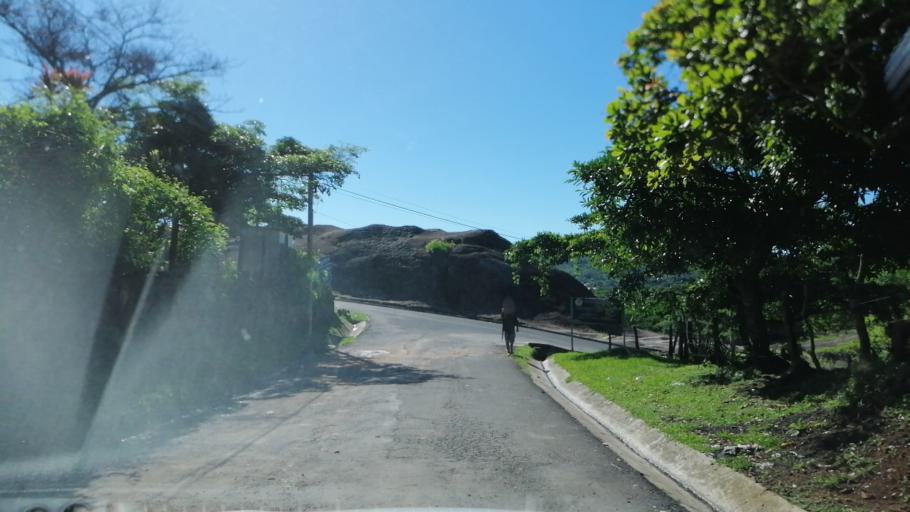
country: SV
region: Morazan
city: Corinto
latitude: 13.8098
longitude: -87.9777
